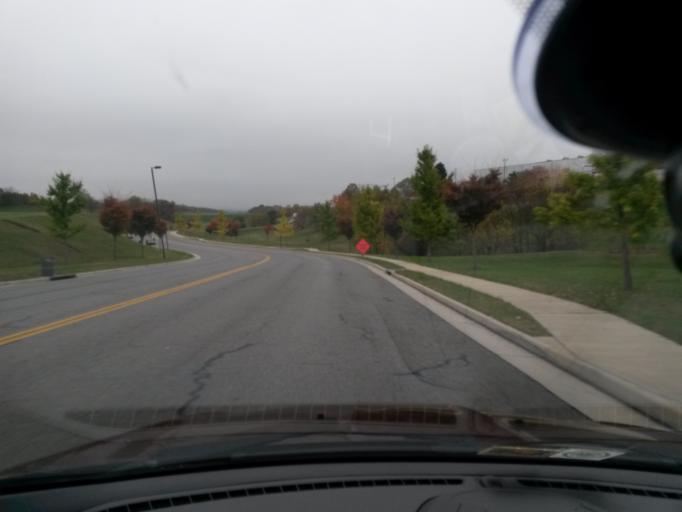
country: US
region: Virginia
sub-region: Roanoke County
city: Vinton
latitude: 37.3075
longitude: -79.9041
